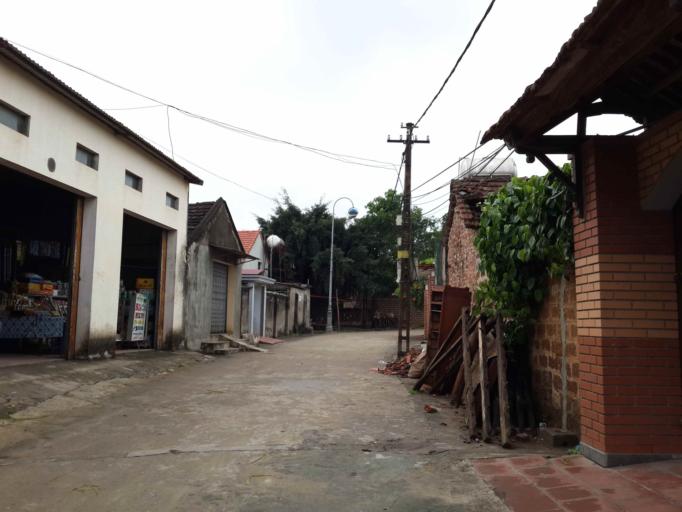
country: VN
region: Ha Noi
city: Son Tay
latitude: 21.1590
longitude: 105.4700
